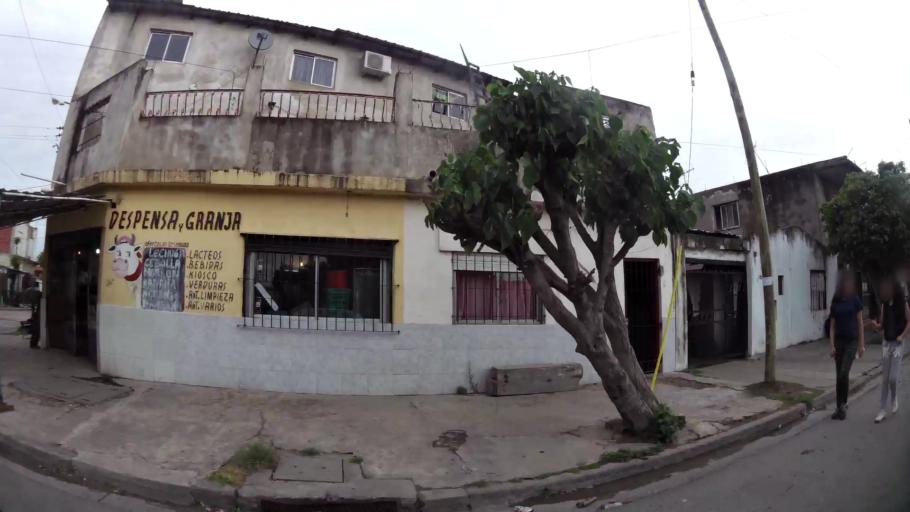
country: AR
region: Buenos Aires
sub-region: Partido de Lanus
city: Lanus
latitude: -34.7261
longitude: -58.3430
